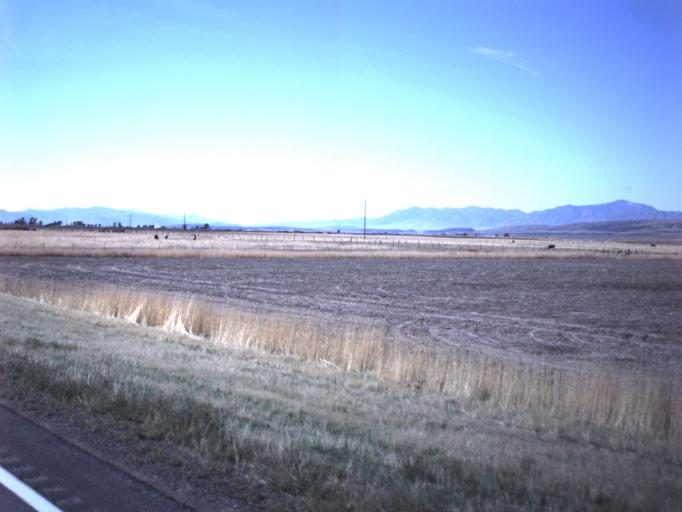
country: US
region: Utah
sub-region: Juab County
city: Nephi
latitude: 39.5809
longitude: -111.8618
